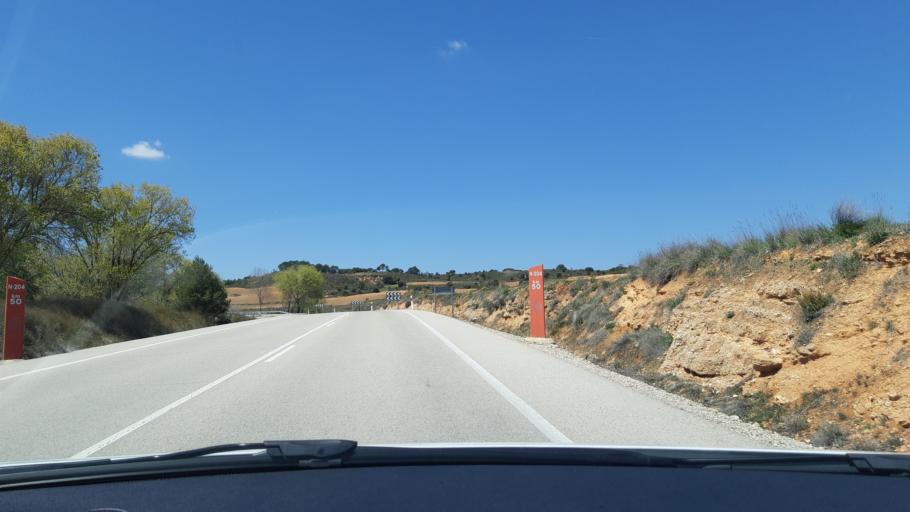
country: ES
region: Castille-La Mancha
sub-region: Provincia de Guadalajara
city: Cifuentes
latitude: 40.7978
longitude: -2.6543
